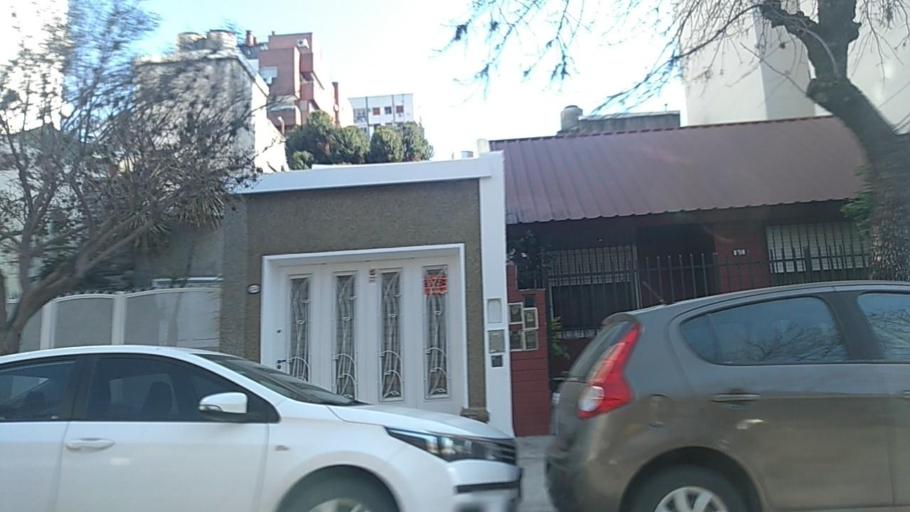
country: AR
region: Buenos Aires F.D.
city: Villa Santa Rita
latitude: -34.6122
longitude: -58.4928
